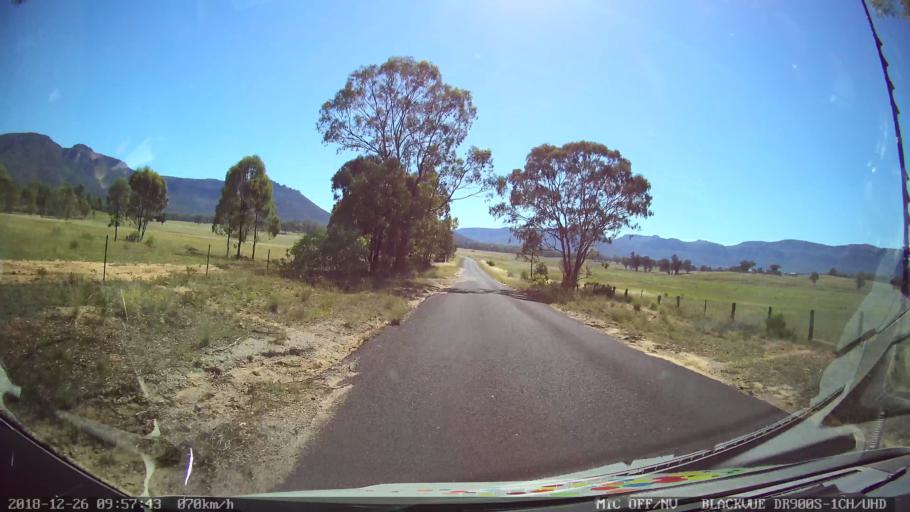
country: AU
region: New South Wales
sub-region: Mid-Western Regional
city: Kandos
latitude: -33.0406
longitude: 150.1959
